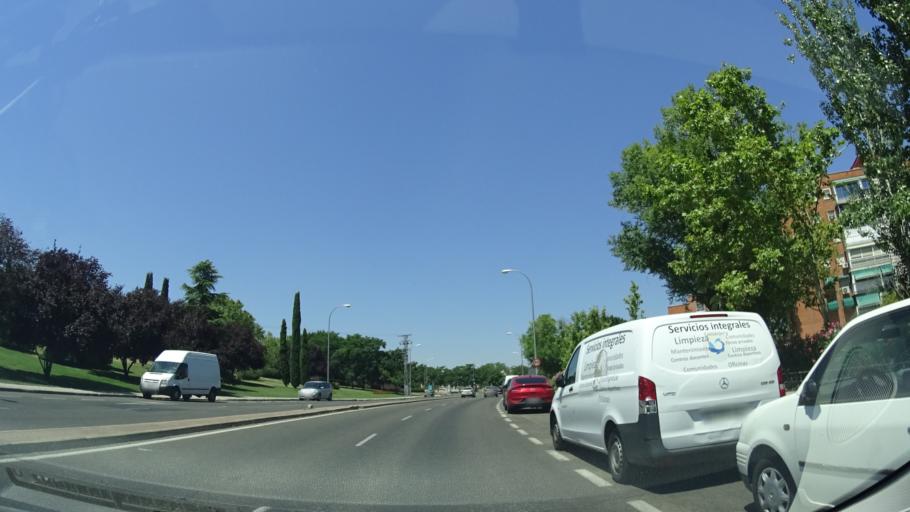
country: ES
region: Madrid
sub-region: Provincia de Madrid
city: Latina
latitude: 40.3772
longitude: -3.7536
